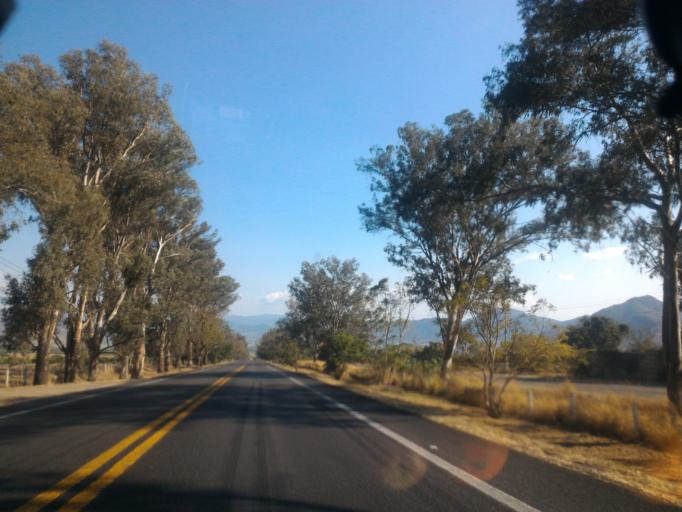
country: MX
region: Jalisco
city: Tuxpan
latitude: 19.5469
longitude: -103.4311
